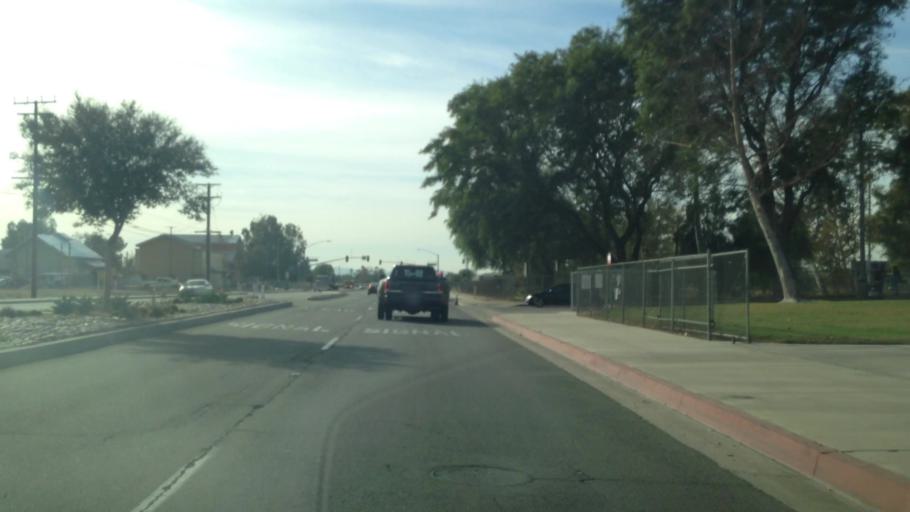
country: US
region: California
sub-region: Riverside County
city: Mira Loma
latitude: 34.0002
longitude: -117.5217
